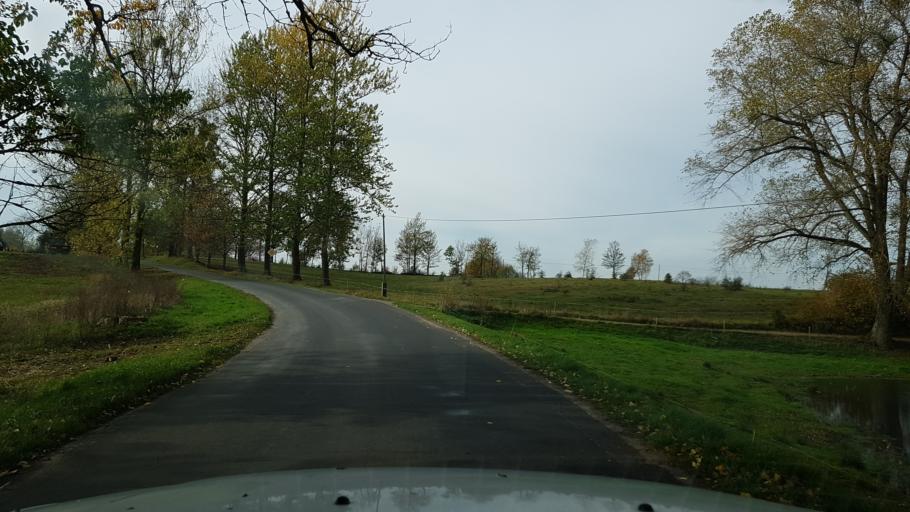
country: PL
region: West Pomeranian Voivodeship
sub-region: Powiat swidwinski
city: Polczyn-Zdroj
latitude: 53.7458
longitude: 16.0395
